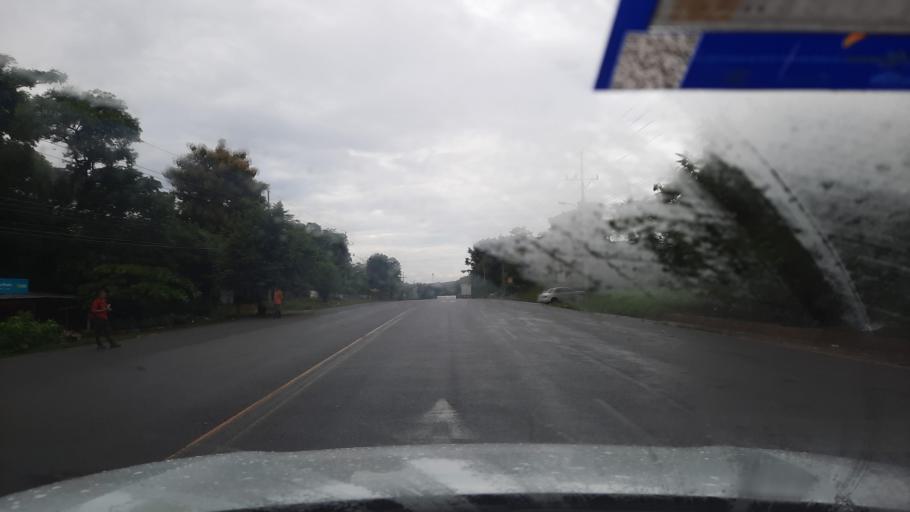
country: NI
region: Rivas
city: Cardenas
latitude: 11.2048
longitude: -85.6160
